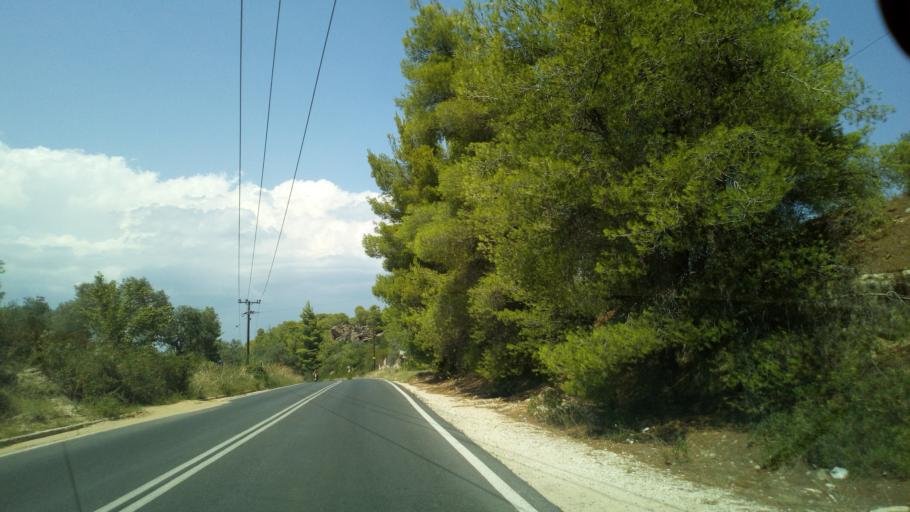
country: GR
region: Central Macedonia
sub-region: Nomos Chalkidikis
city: Agios Nikolaos
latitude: 40.2111
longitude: 23.7567
